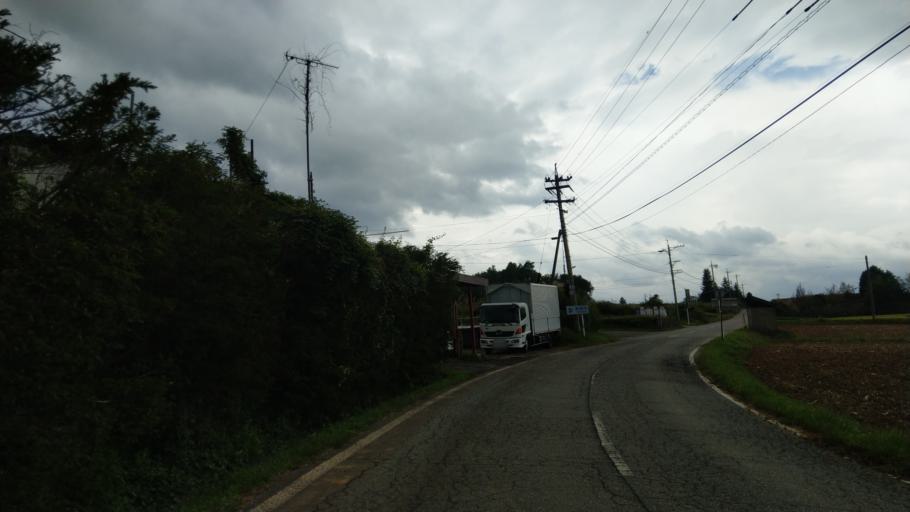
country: JP
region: Nagano
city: Komoro
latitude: 36.3011
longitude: 138.3845
